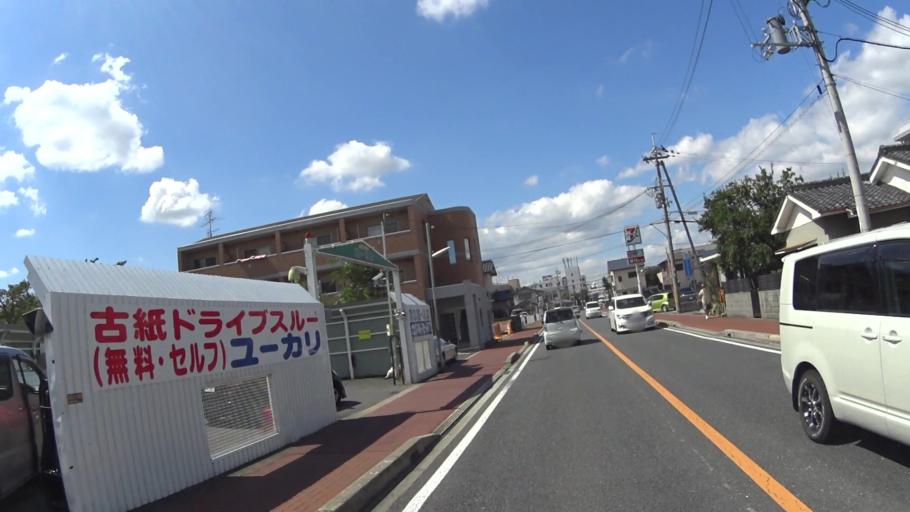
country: JP
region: Kyoto
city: Uji
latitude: 34.8932
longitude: 135.7873
